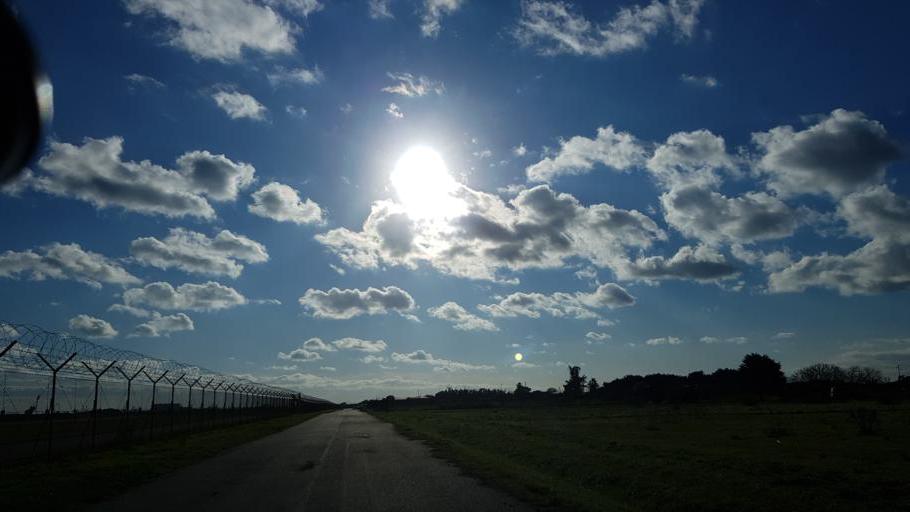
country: IT
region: Apulia
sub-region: Provincia di Brindisi
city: Materdomini
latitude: 40.6678
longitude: 17.9325
